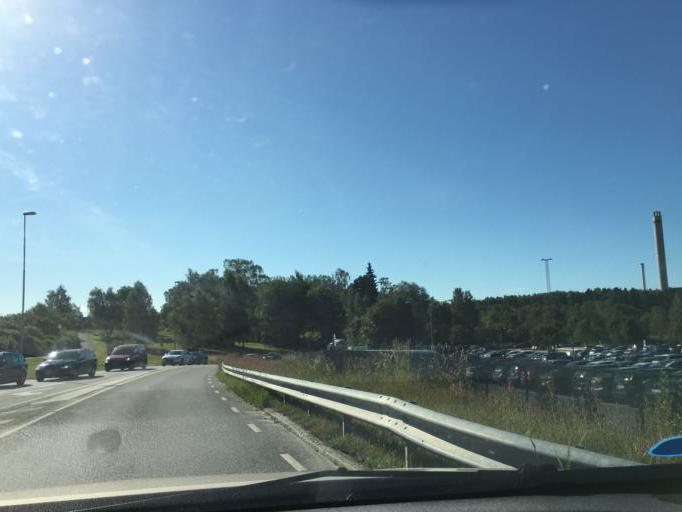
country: SE
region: Stockholm
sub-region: Sodertalje Kommun
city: Pershagen
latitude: 59.1847
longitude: 17.6621
